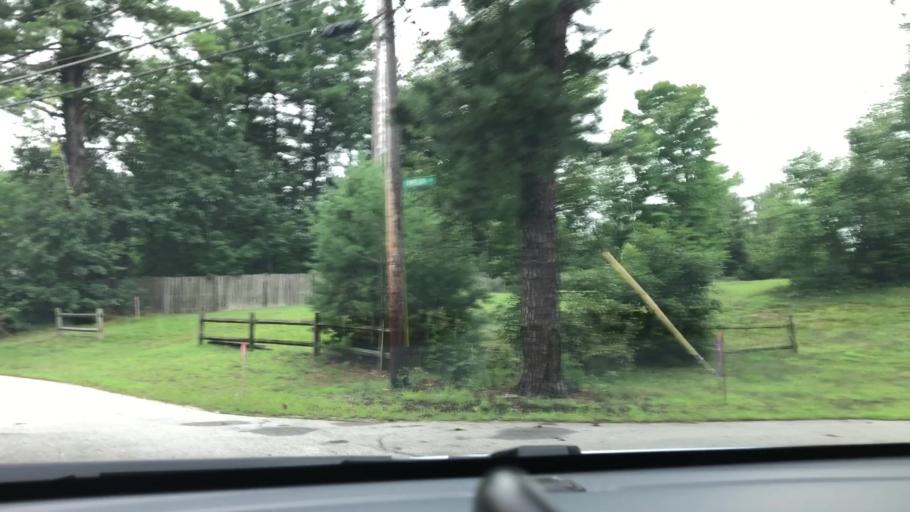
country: US
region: New Hampshire
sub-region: Hillsborough County
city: Pinardville
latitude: 43.0066
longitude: -71.5222
